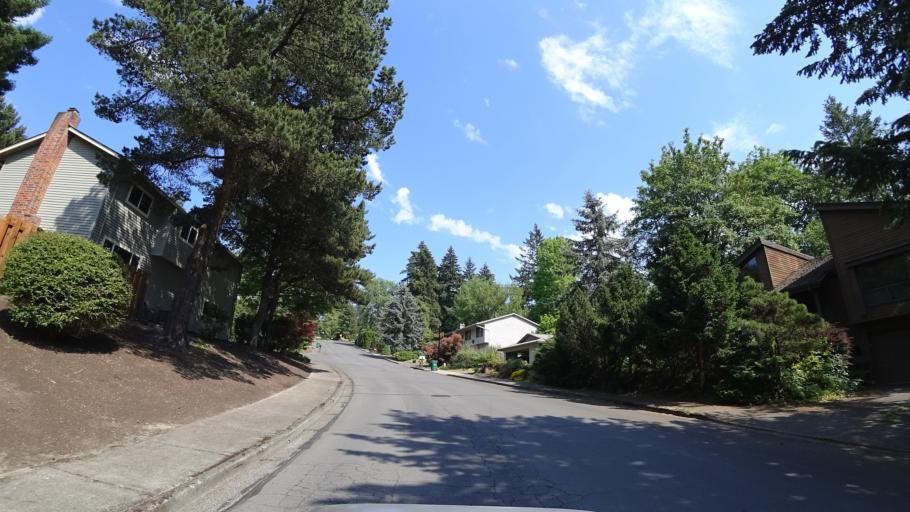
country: US
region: Oregon
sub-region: Washington County
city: Metzger
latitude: 45.4500
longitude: -122.7500
